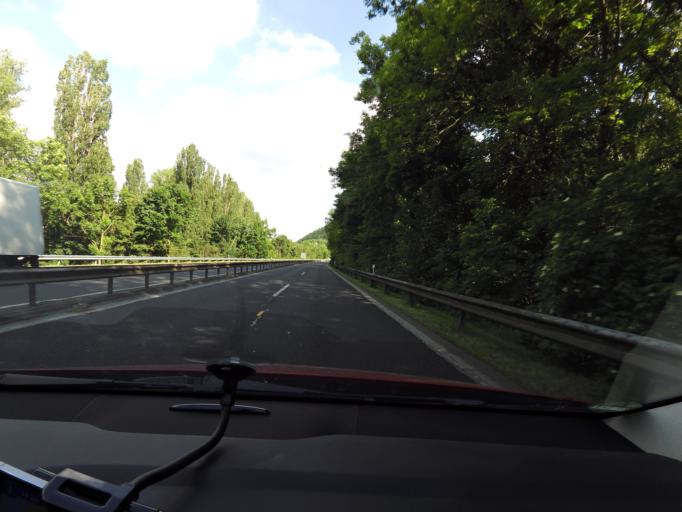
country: DE
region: Rheinland-Pfalz
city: Leutesdorf
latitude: 50.4509
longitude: 7.3727
